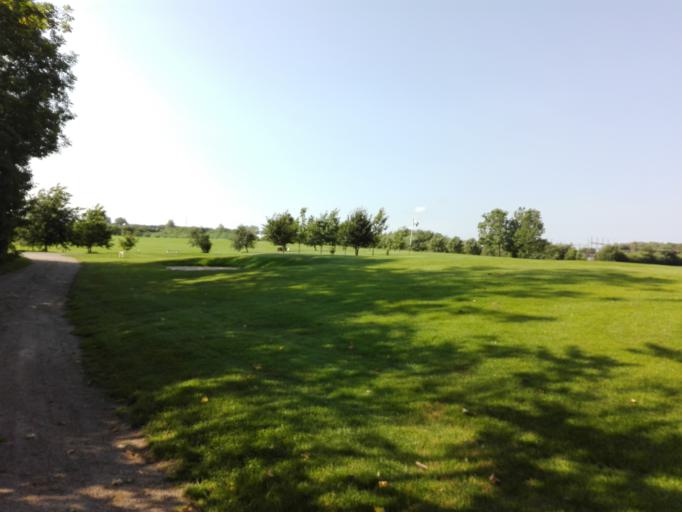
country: DK
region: Central Jutland
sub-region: Arhus Kommune
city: Lystrup
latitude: 56.2131
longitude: 10.1937
